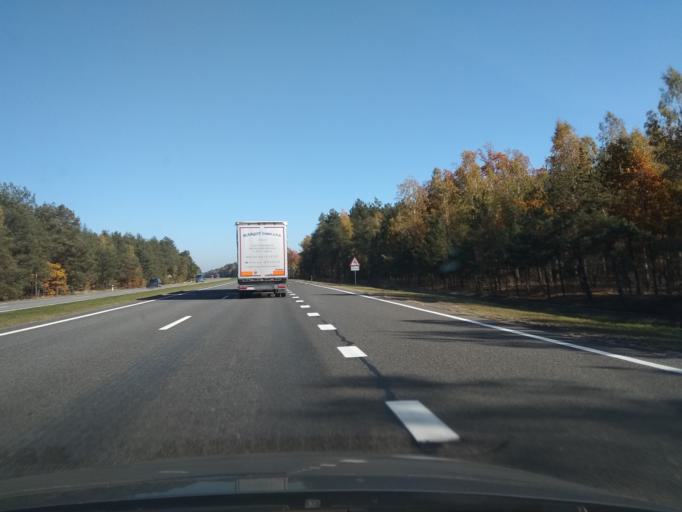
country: BY
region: Brest
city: Antopal'
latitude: 52.3660
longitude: 24.7341
